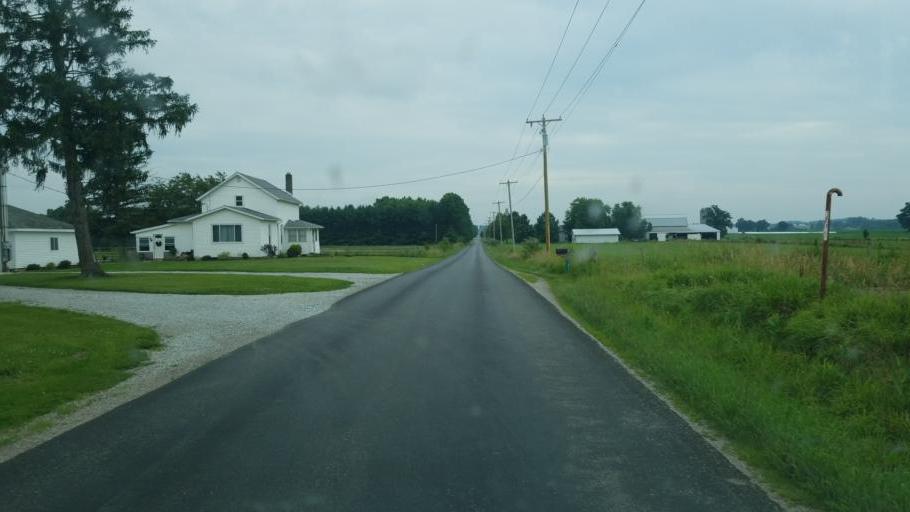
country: US
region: Ohio
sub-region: Wayne County
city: Orrville
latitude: 40.8123
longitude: -81.7750
